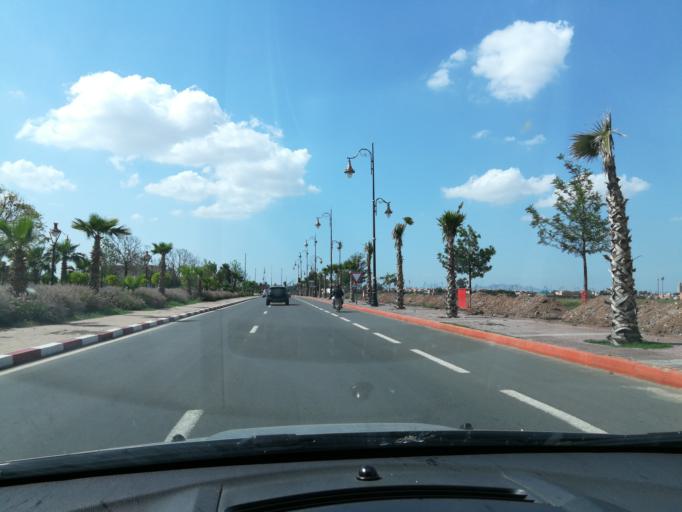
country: MA
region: Marrakech-Tensift-Al Haouz
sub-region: Marrakech
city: Marrakesh
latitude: 31.6021
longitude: -7.9976
